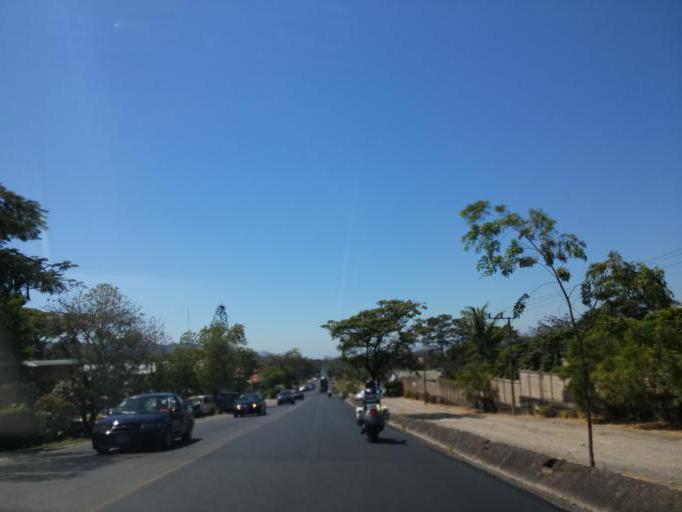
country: CR
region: Heredia
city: Colon
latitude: 9.9346
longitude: -84.2238
